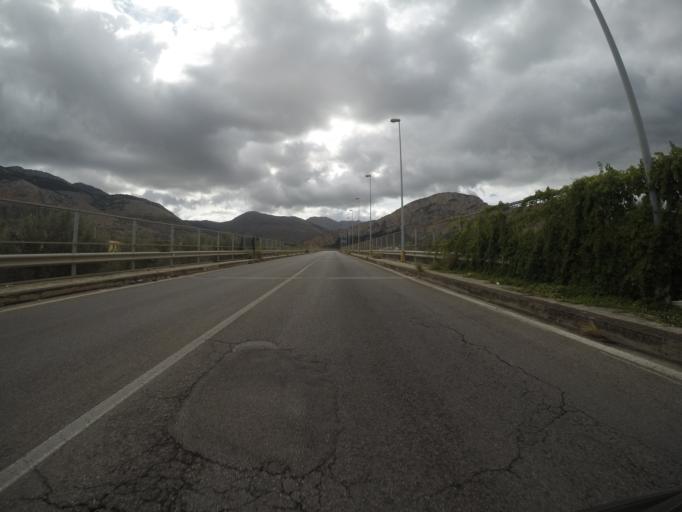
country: IT
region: Sicily
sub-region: Palermo
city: Capaci
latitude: 38.1696
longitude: 13.2210
